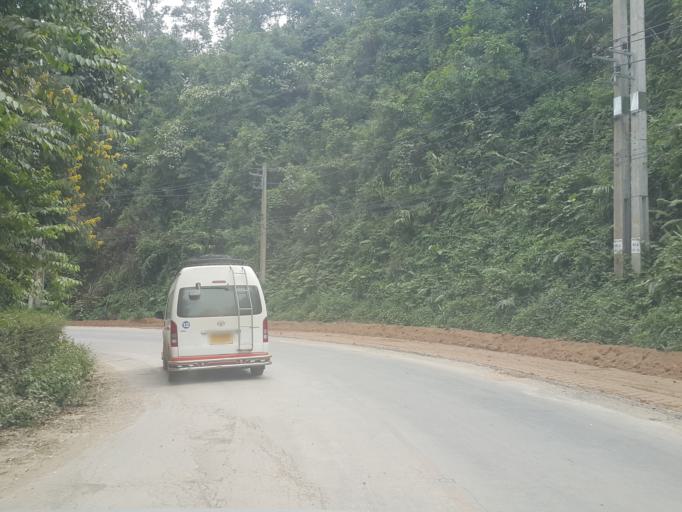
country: TH
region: Chiang Mai
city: Mae Taeng
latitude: 19.1316
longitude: 98.7040
